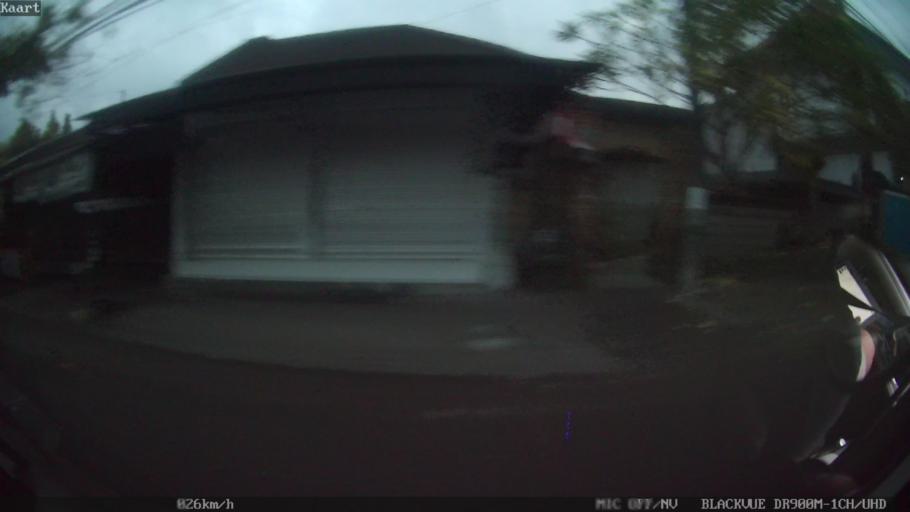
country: ID
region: Bali
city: Banjar Parekan
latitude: -8.5645
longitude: 115.2207
